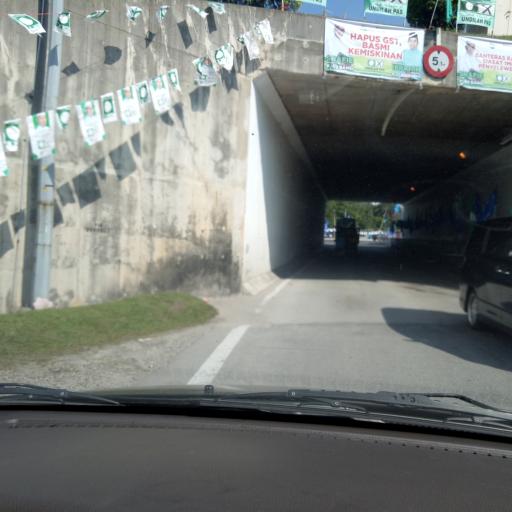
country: MY
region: Selangor
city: Kampong Baharu Balakong
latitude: 3.0137
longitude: 101.7688
